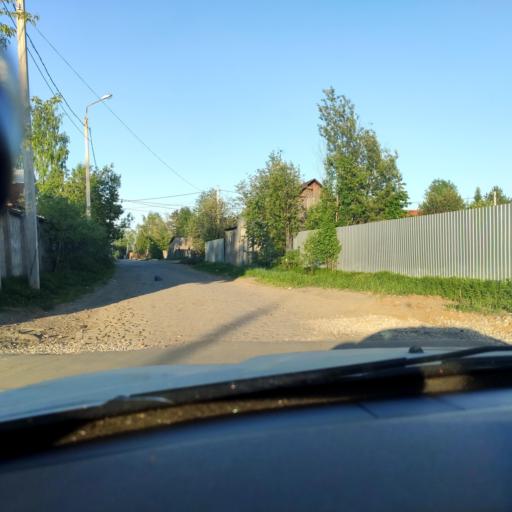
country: RU
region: Perm
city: Polazna
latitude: 58.1402
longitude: 56.4497
